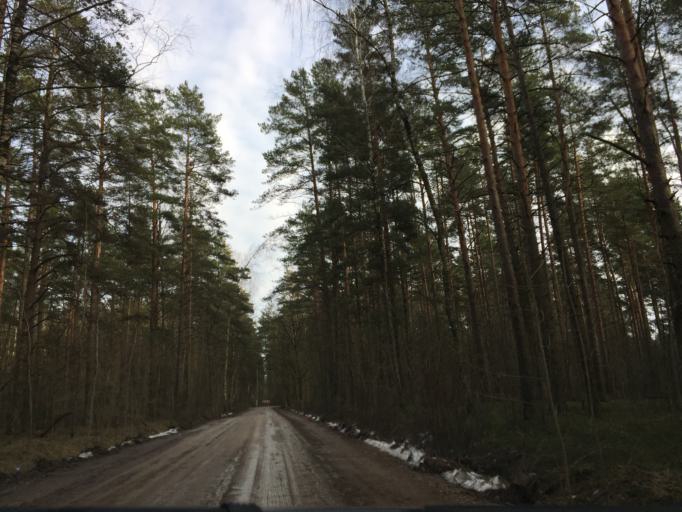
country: LV
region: Stopini
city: Ulbroka
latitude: 56.9222
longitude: 24.2971
